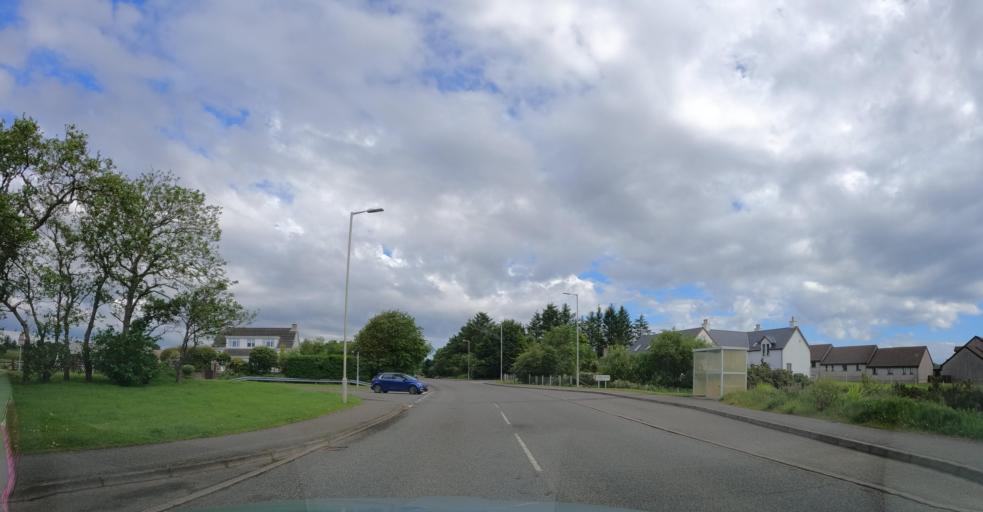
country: GB
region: Scotland
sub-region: Eilean Siar
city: Isle of Lewis
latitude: 58.2237
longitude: -6.3860
